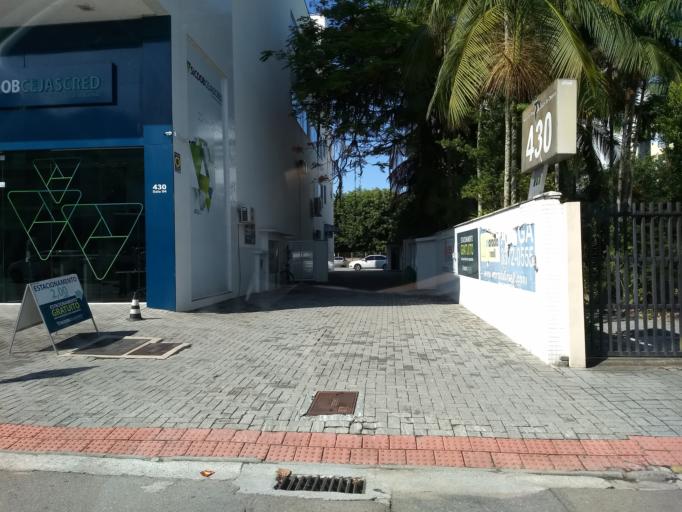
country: BR
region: Santa Catarina
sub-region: Jaragua Do Sul
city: Jaragua do Sul
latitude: -26.4841
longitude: -49.0795
